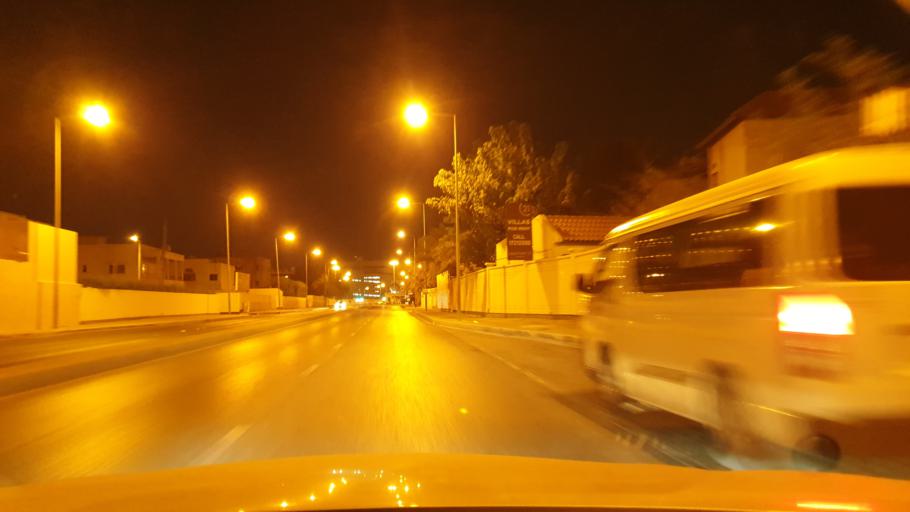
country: BH
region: Manama
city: Manama
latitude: 26.2167
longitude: 50.5803
